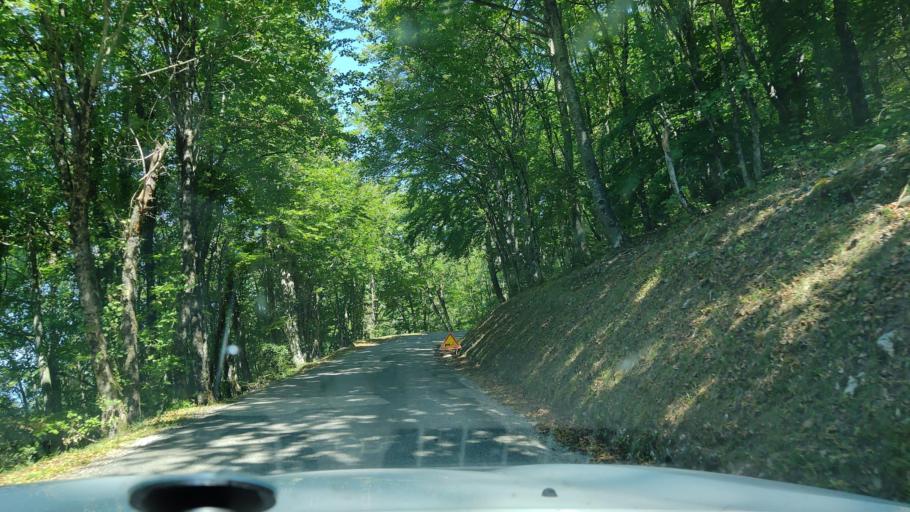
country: FR
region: Rhone-Alpes
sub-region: Departement de la Savoie
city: Novalaise
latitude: 45.6479
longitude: 5.7984
